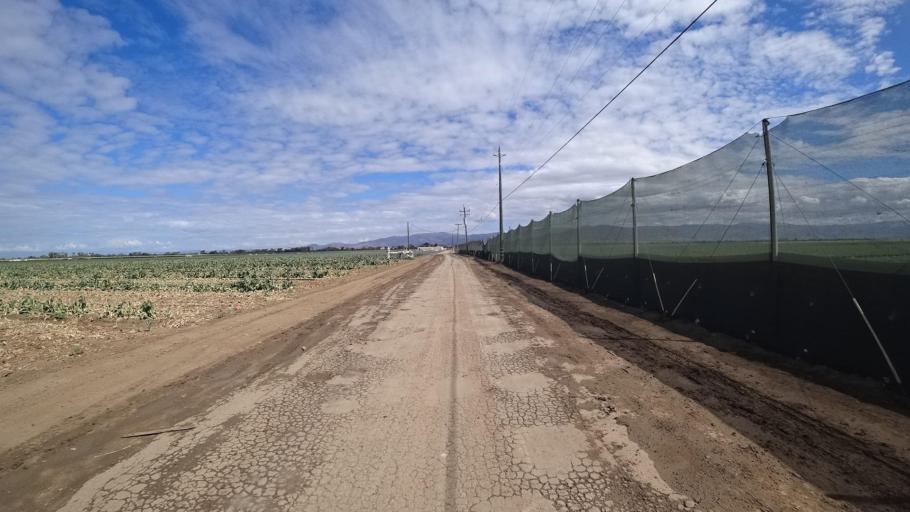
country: US
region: California
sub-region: Monterey County
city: Chualar
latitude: 36.6007
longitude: -121.6024
